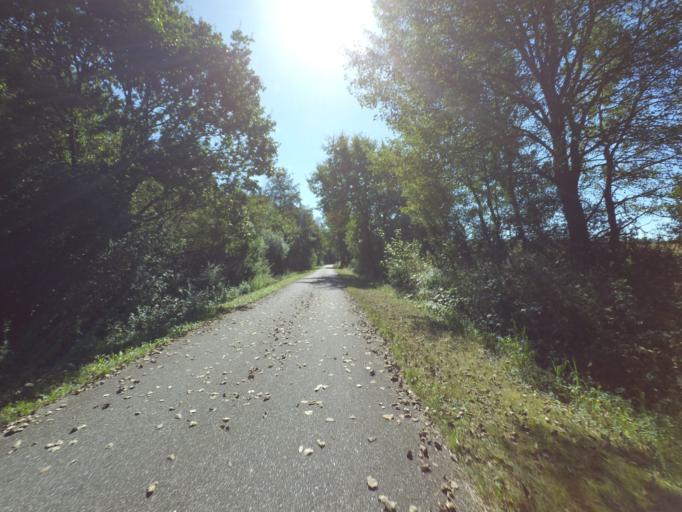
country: DE
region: Rheinland-Pfalz
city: Niederofflingen
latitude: 50.0696
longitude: 6.8908
